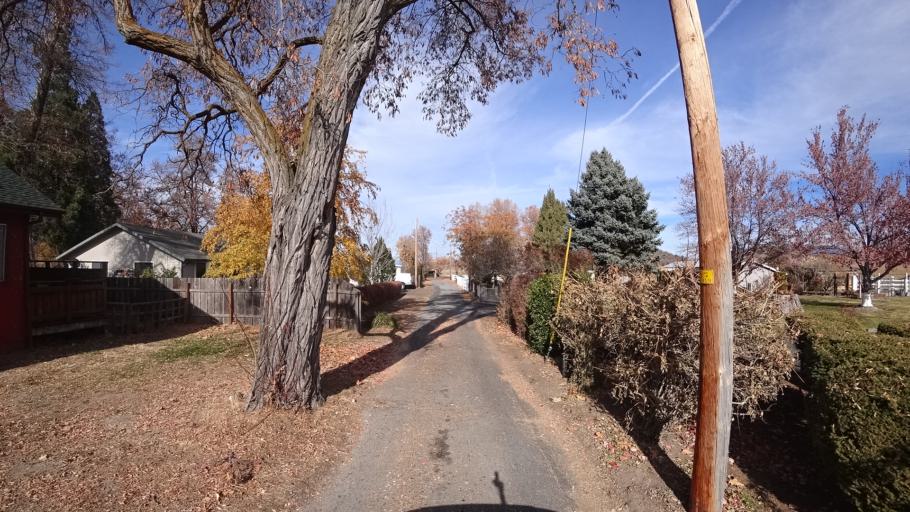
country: US
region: California
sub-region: Siskiyou County
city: Weed
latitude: 41.4590
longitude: -122.4309
